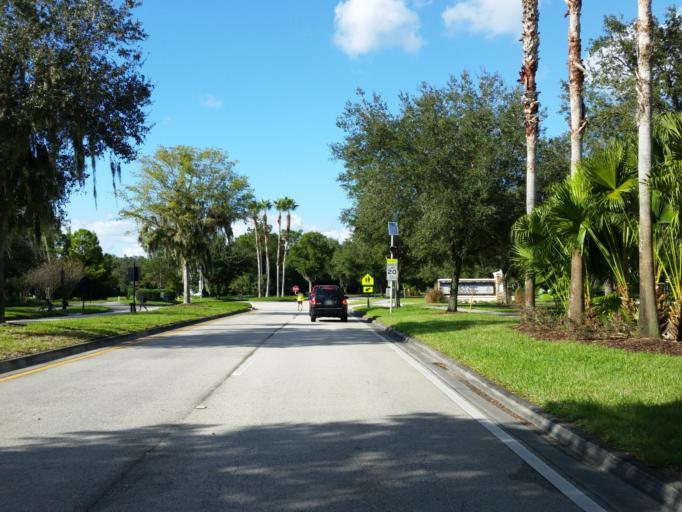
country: US
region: Florida
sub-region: Hillsborough County
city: Fish Hawk
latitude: 27.8483
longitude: -82.2327
